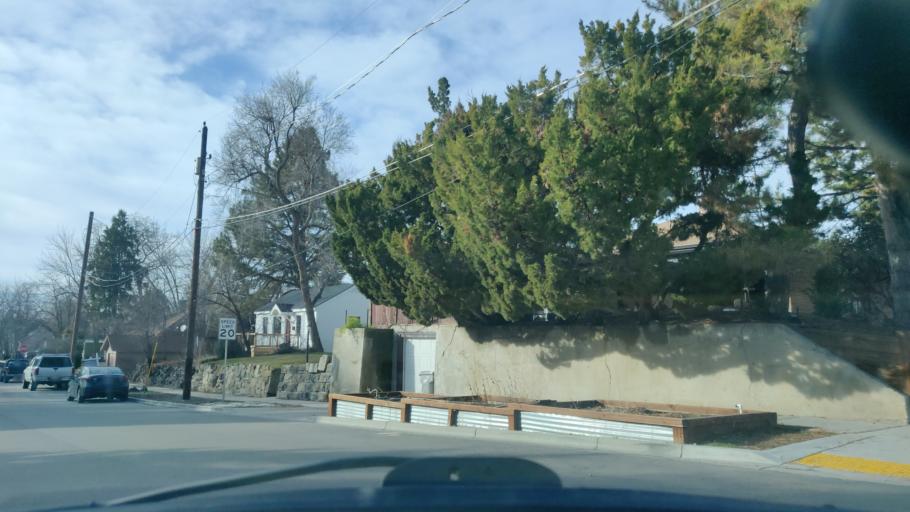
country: US
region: Idaho
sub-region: Ada County
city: Boise
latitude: 43.6328
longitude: -116.1976
